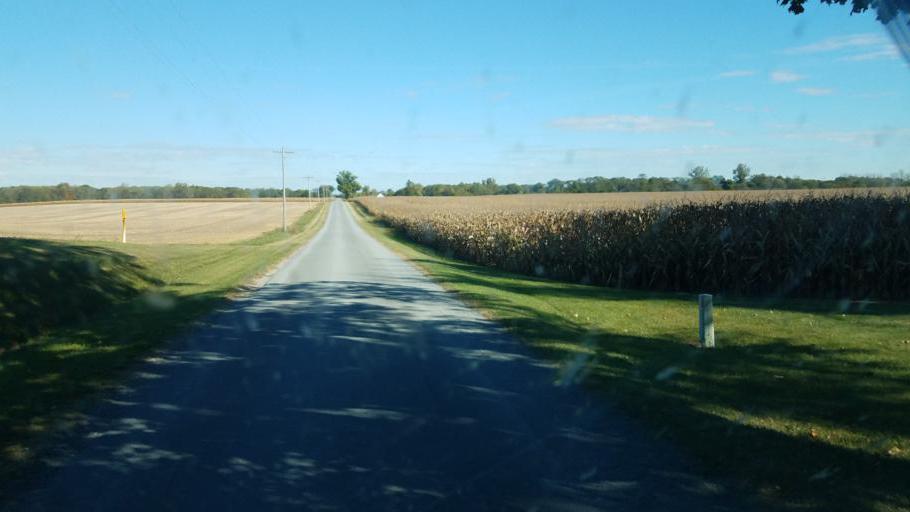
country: US
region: Ohio
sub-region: Wyandot County
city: Upper Sandusky
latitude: 40.7193
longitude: -83.2072
